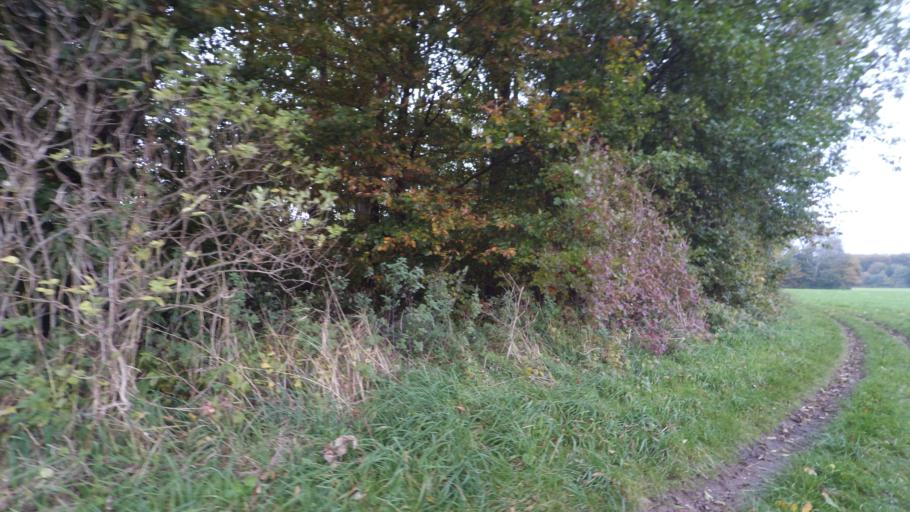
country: DK
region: Central Jutland
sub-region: Arhus Kommune
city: Stavtrup
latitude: 56.1342
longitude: 10.0895
